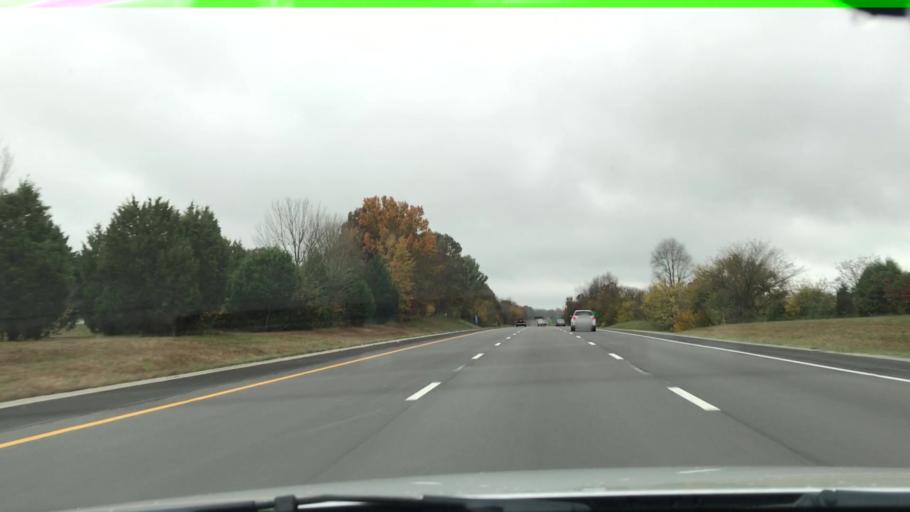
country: US
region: Kentucky
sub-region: Warren County
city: Bowling Green
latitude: 37.0171
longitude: -86.2757
